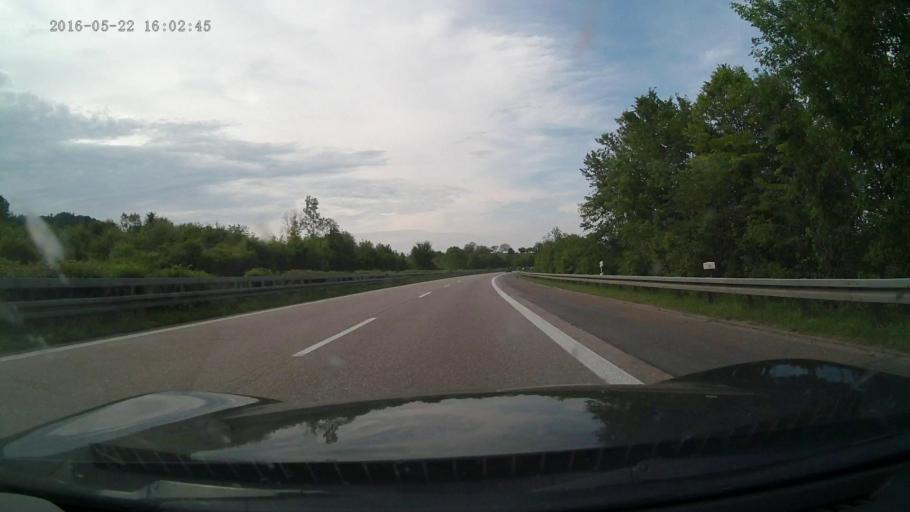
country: DE
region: Baden-Wuerttemberg
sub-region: Regierungsbezirk Stuttgart
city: Eberstadt
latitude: 49.2039
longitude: 9.3448
